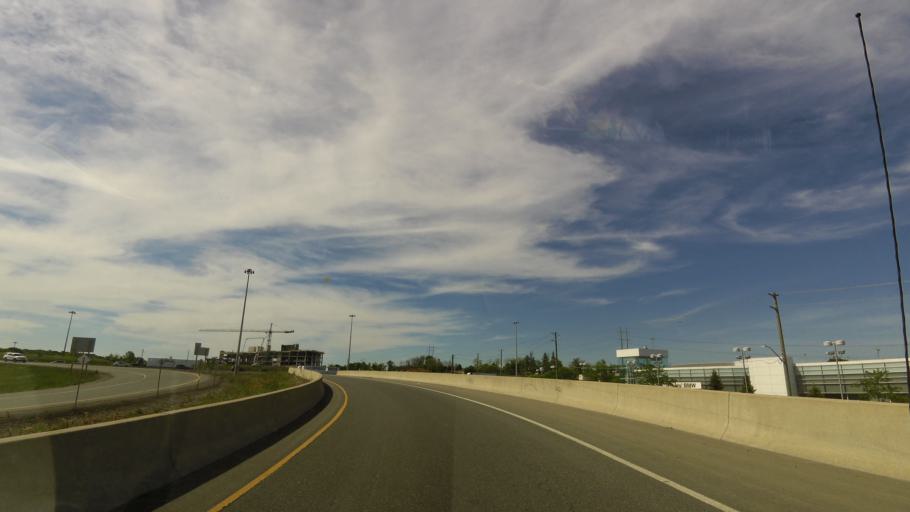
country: CA
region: Ontario
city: Oakville
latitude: 43.4103
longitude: -79.7371
